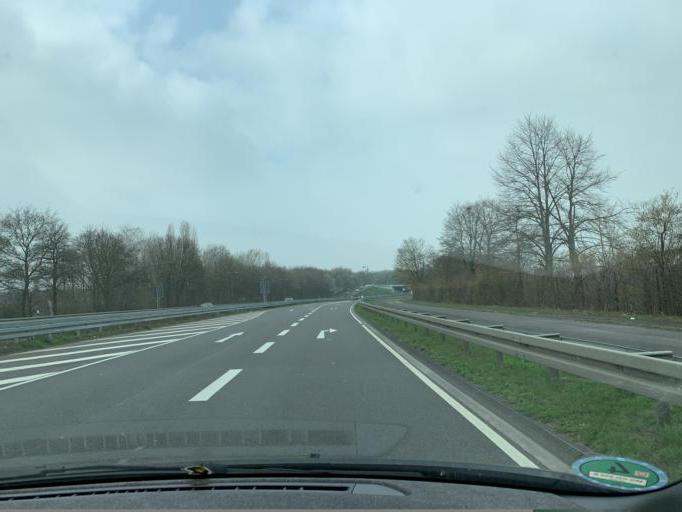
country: DE
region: North Rhine-Westphalia
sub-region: Regierungsbezirk Koln
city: Bilderstoeckchen
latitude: 51.0283
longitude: 6.9222
